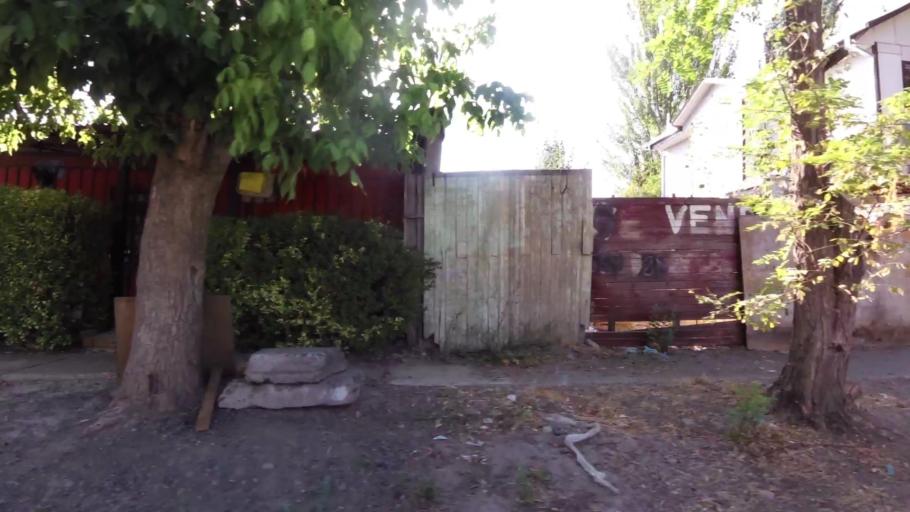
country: CL
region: Maule
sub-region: Provincia de Talca
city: Talca
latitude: -35.4029
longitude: -71.6611
